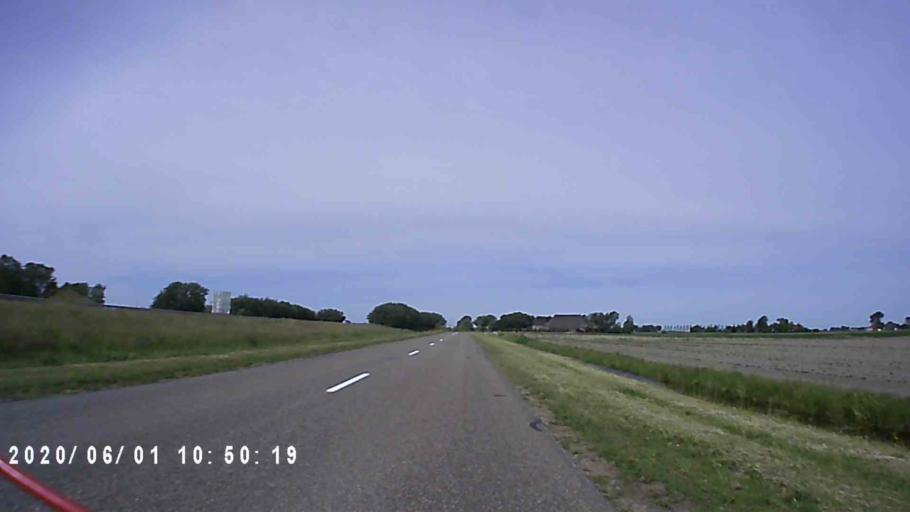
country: NL
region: Friesland
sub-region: Gemeente Franekeradeel
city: Franeker
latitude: 53.1990
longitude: 5.5247
